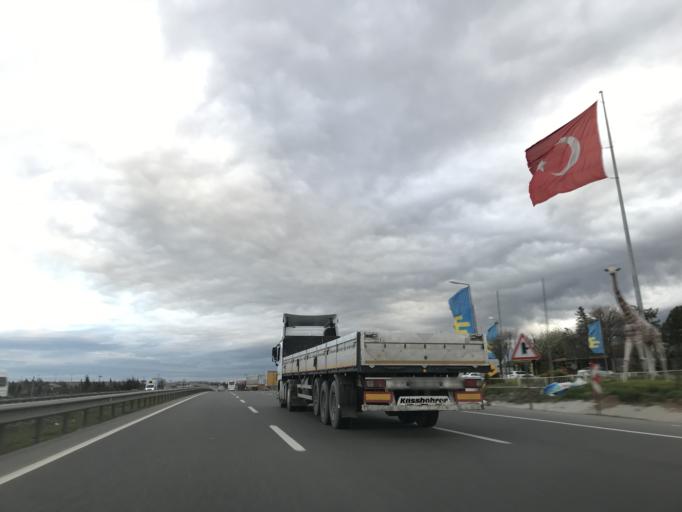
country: TR
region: Ankara
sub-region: Goelbasi
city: Golbasi
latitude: 39.7592
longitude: 32.8043
